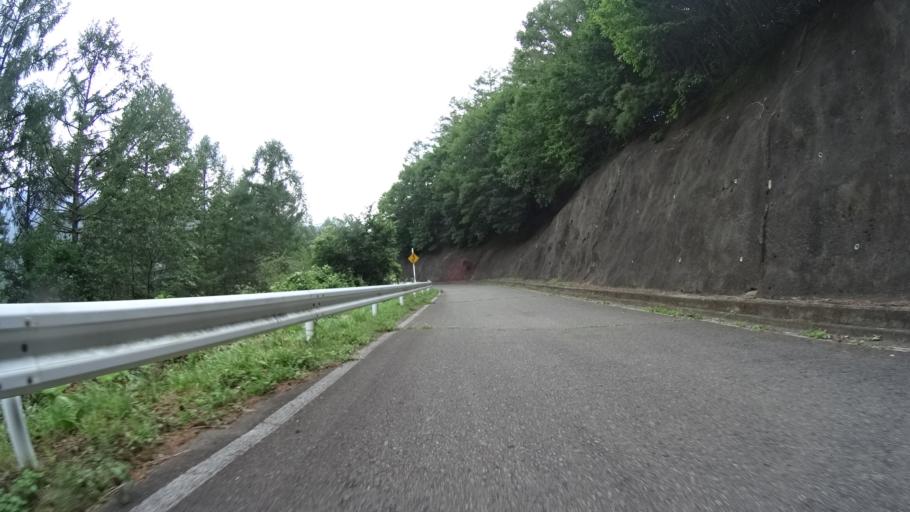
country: JP
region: Nagano
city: Saku
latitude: 36.0679
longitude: 138.6381
